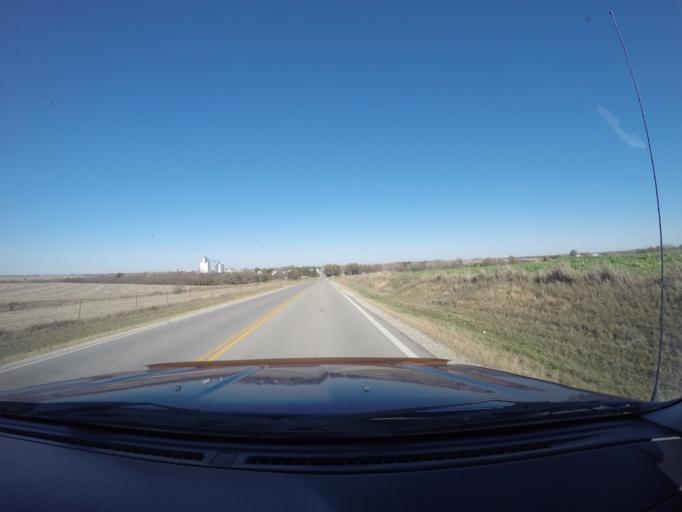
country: US
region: Kansas
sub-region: Marshall County
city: Marysville
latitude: 39.8532
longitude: -96.4170
